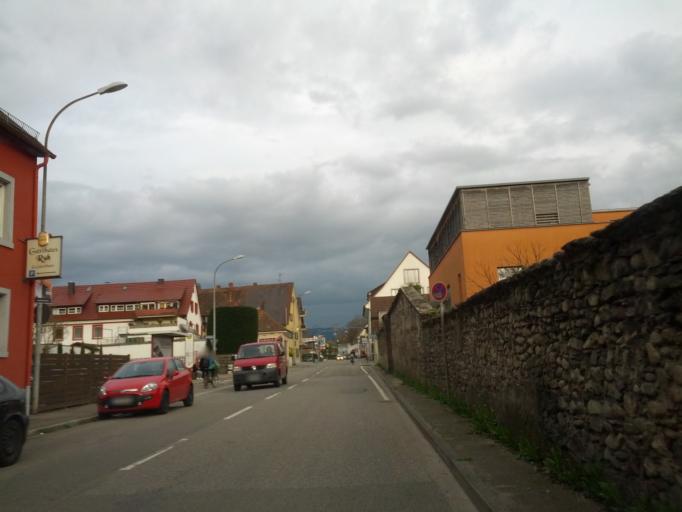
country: DE
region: Baden-Wuerttemberg
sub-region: Freiburg Region
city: Kirchzarten
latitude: 47.9870
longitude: 7.9031
